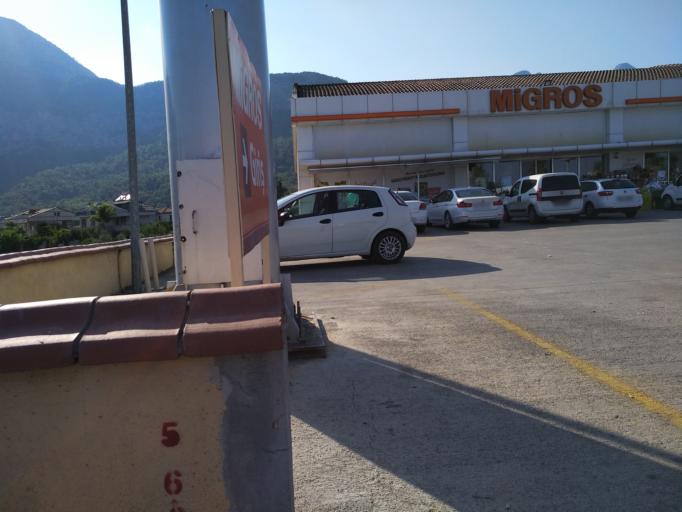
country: TR
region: Antalya
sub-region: Kemer
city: Goeynuek
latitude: 36.6656
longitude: 30.5507
